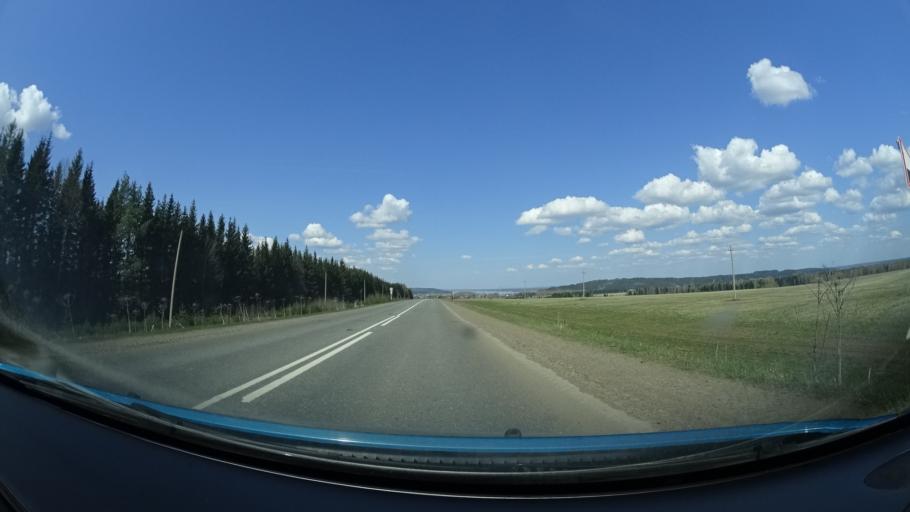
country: RU
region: Perm
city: Osa
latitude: 57.2704
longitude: 55.5709
